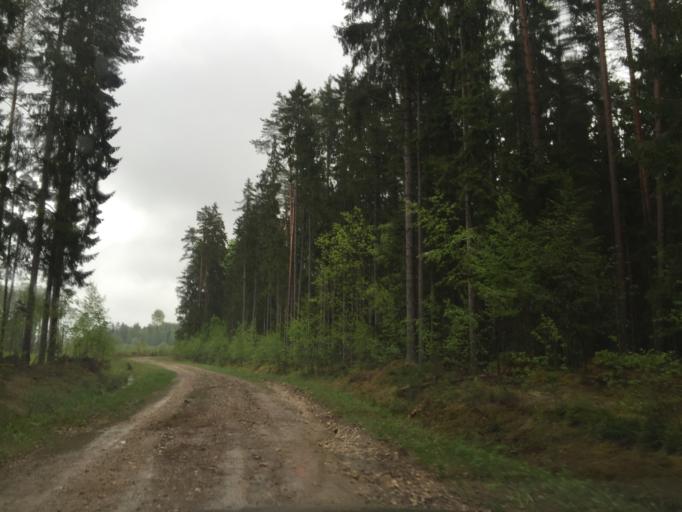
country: LV
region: Ogre
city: Jumprava
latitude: 56.6775
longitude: 24.9273
